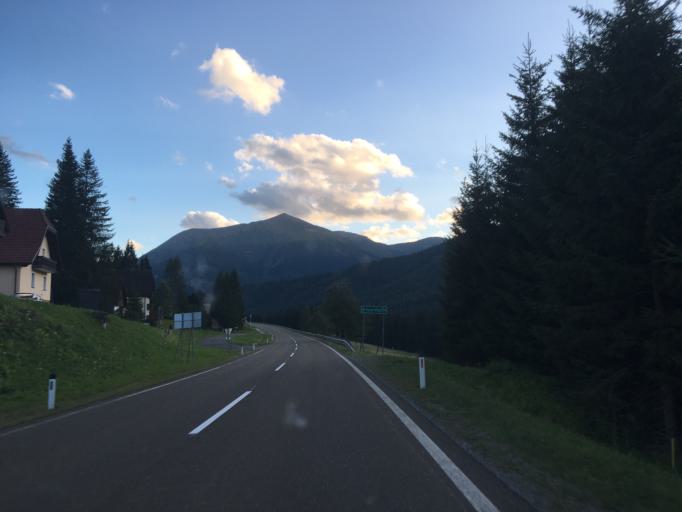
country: AT
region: Styria
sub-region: Politischer Bezirk Murtal
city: Hohentauern
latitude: 47.4303
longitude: 14.4671
